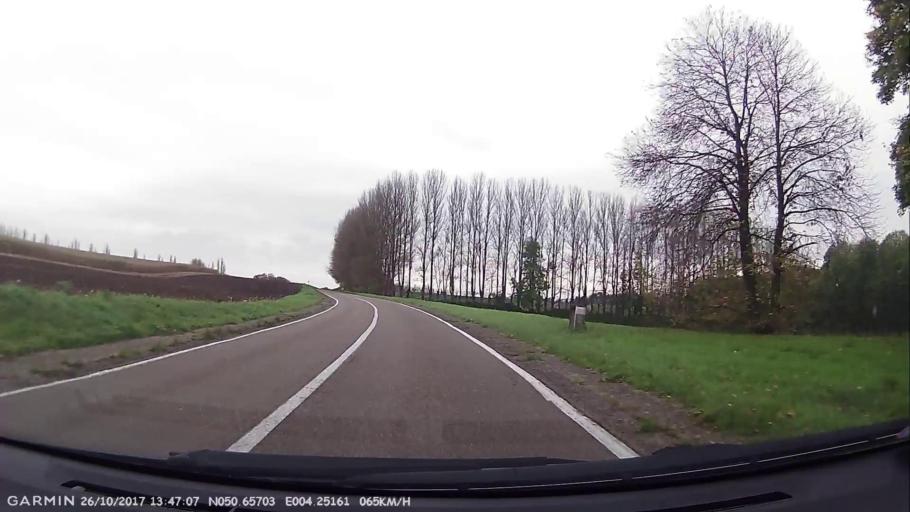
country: BE
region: Wallonia
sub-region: Province du Brabant Wallon
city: Ittre
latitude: 50.6567
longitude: 4.2518
